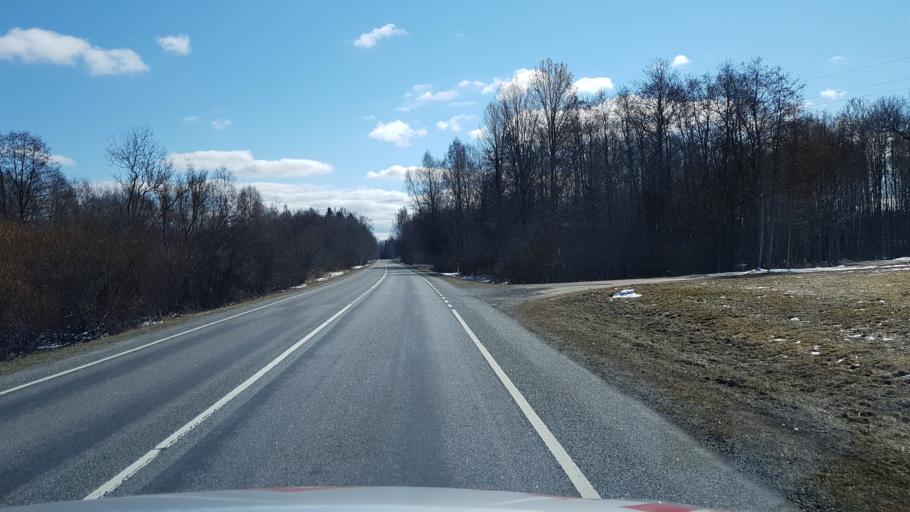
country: EE
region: Laeaene-Virumaa
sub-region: Tapa vald
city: Tapa
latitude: 59.4449
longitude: 25.9513
